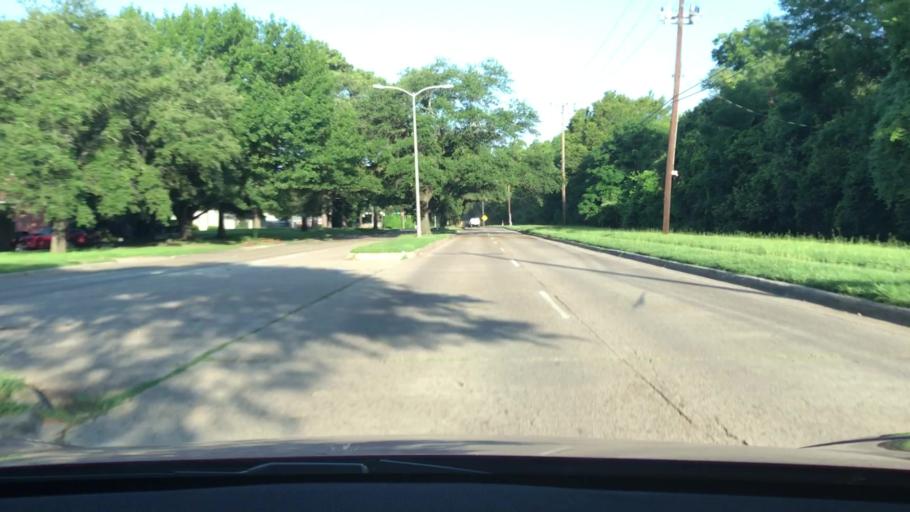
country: US
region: Louisiana
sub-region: Bossier Parish
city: Bossier City
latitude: 32.4567
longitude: -93.7258
